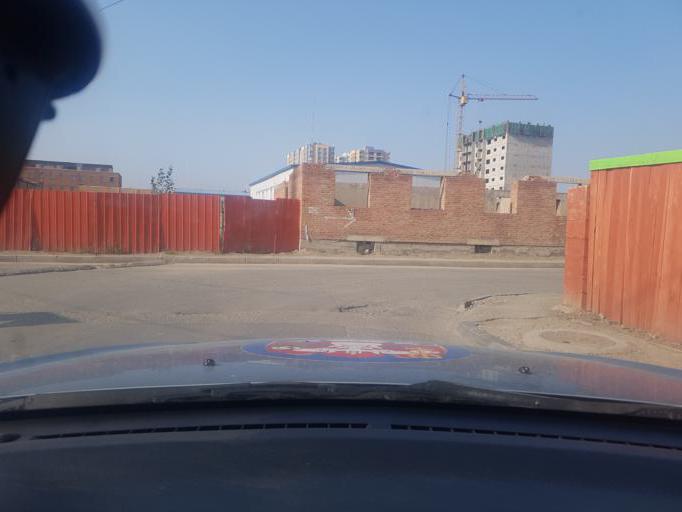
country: MN
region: Ulaanbaatar
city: Ulaanbaatar
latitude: 47.9215
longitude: 106.9657
